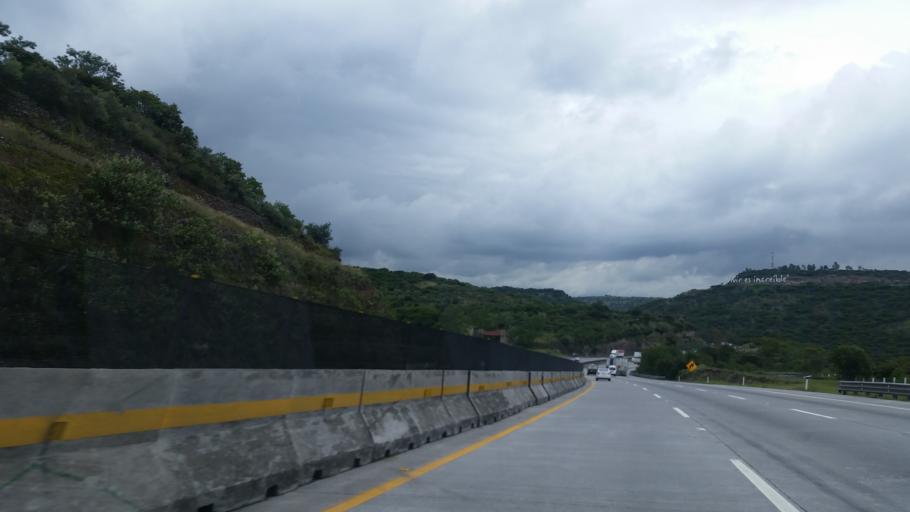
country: MX
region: Hidalgo
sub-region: Tepeji del Rio de Ocampo
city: Santiago Tlautla
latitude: 19.9537
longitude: -99.4080
